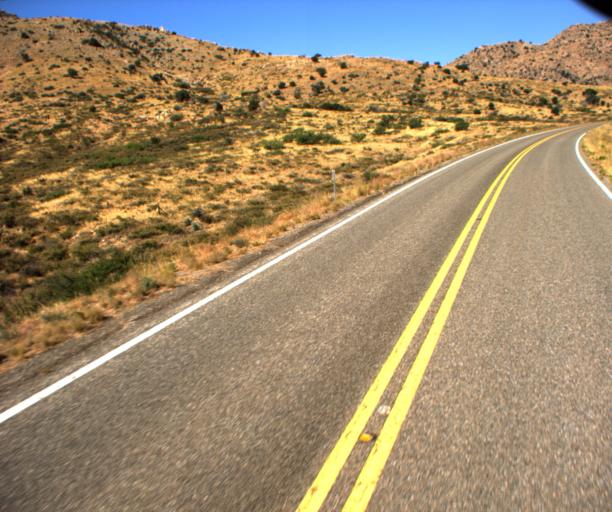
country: US
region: Arizona
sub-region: Graham County
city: Swift Trail Junction
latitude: 32.5603
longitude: -109.7834
